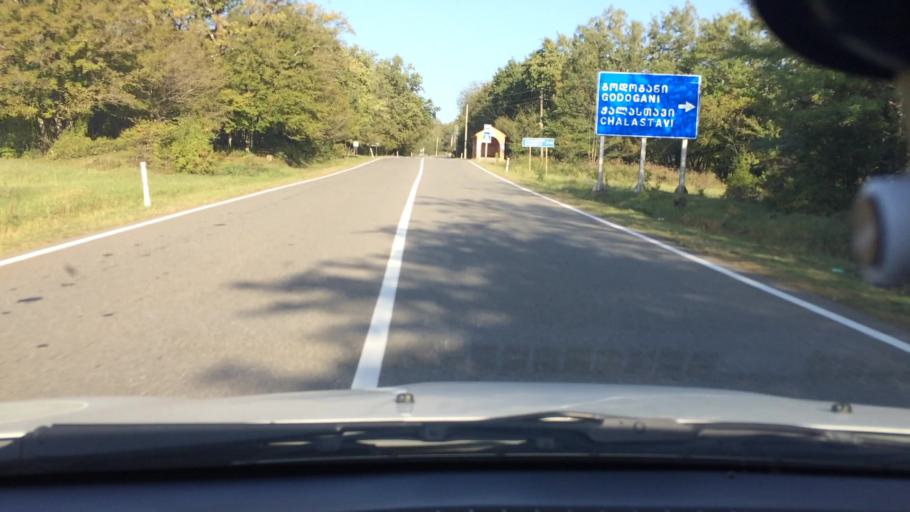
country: GE
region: Imereti
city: Kutaisi
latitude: 42.2452
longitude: 42.7594
